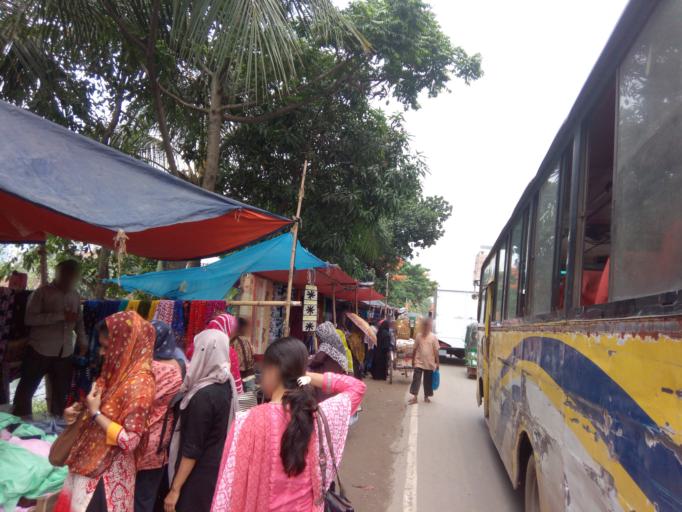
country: BD
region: Dhaka
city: Paltan
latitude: 23.7623
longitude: 90.4415
